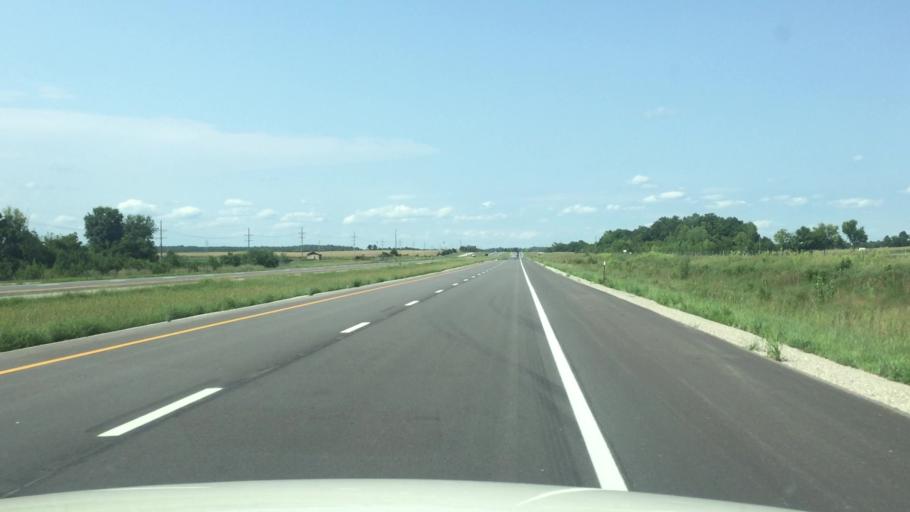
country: US
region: Kansas
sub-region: Linn County
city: La Cygne
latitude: 38.3120
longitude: -94.6775
